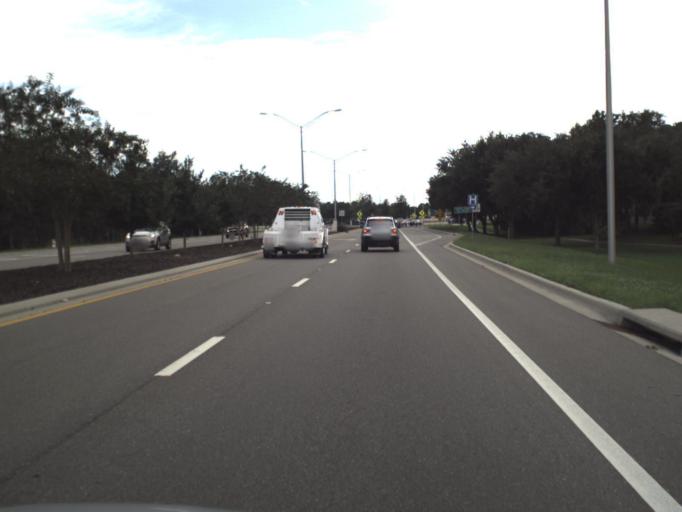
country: US
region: Florida
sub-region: Sarasota County
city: Plantation
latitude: 27.1020
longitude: -82.3845
